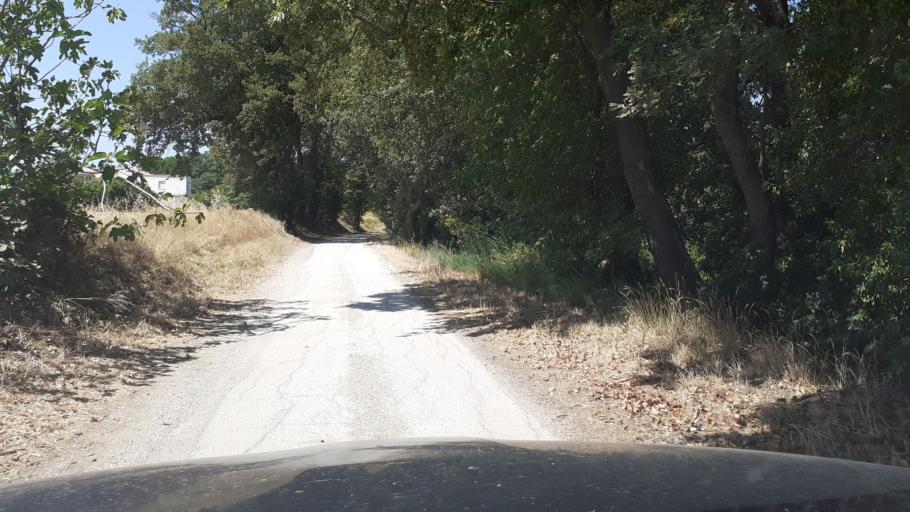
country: IT
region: Abruzzo
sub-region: Provincia di Chieti
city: Santa Maria Imbaro
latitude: 42.2095
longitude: 14.4759
